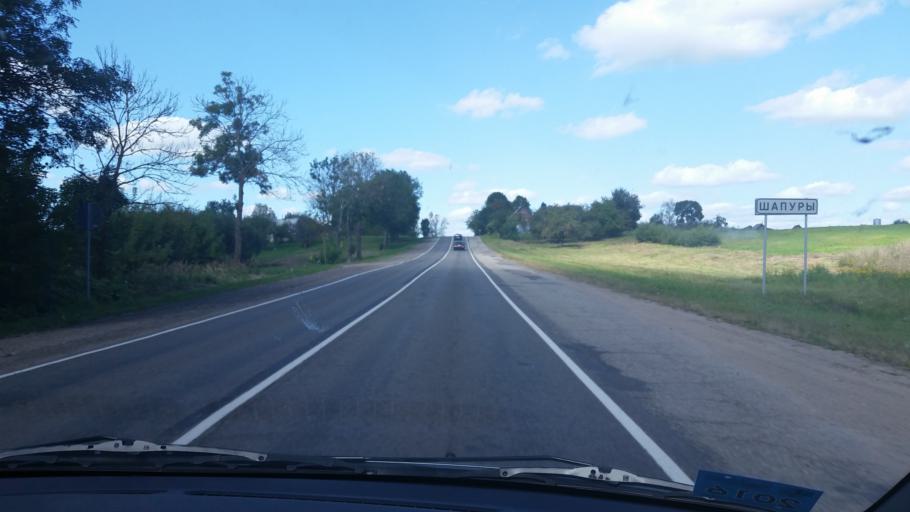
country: BY
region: Vitebsk
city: Vitebsk
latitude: 55.1091
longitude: 30.2833
